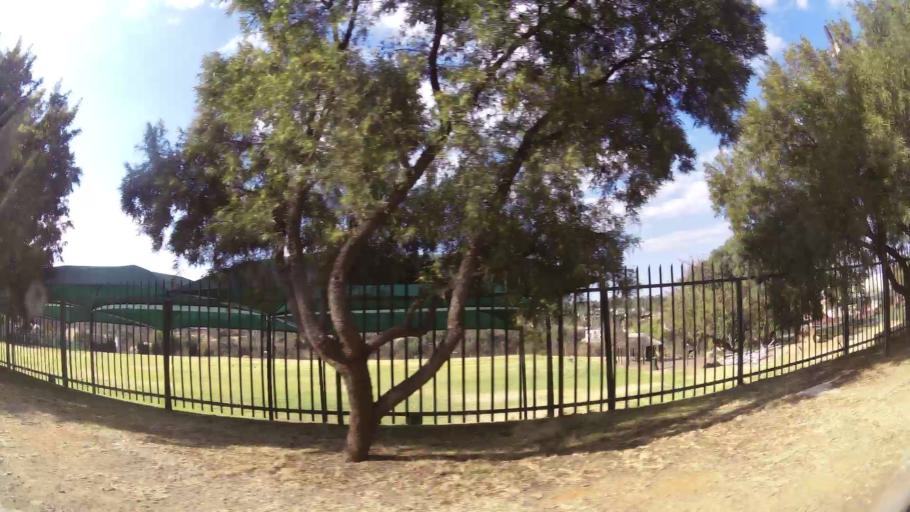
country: ZA
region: Gauteng
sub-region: City of Johannesburg Metropolitan Municipality
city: Diepsloot
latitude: -26.0073
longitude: 28.0318
